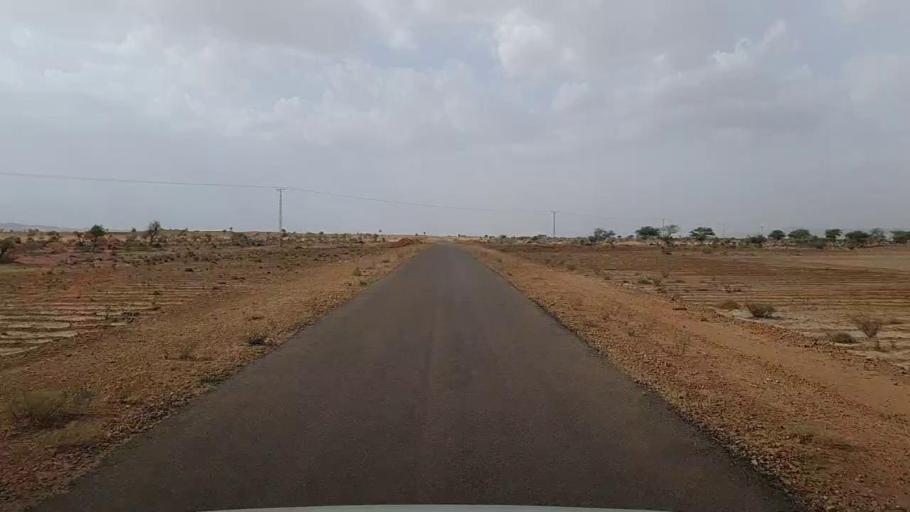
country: PK
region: Sindh
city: Jamshoro
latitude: 25.4612
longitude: 67.6774
